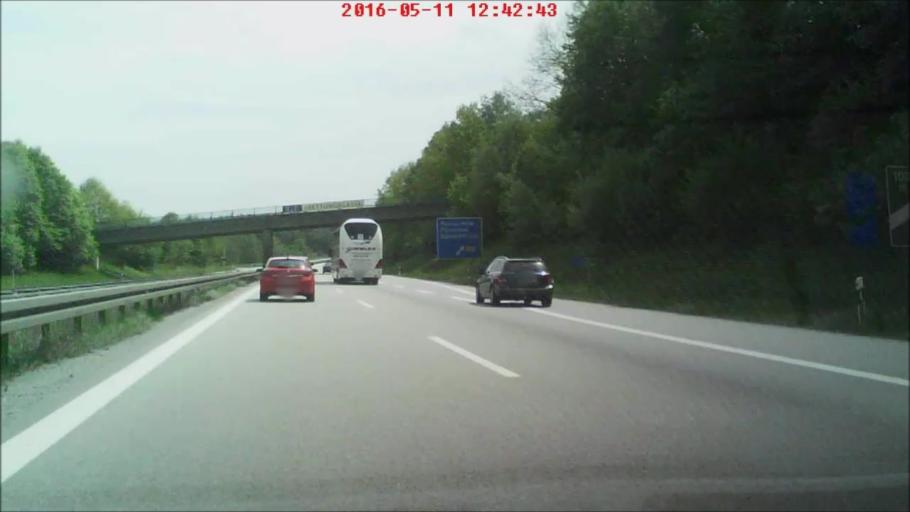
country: DE
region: Bavaria
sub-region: Lower Bavaria
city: Tiefenbach
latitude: 48.5694
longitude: 13.3768
